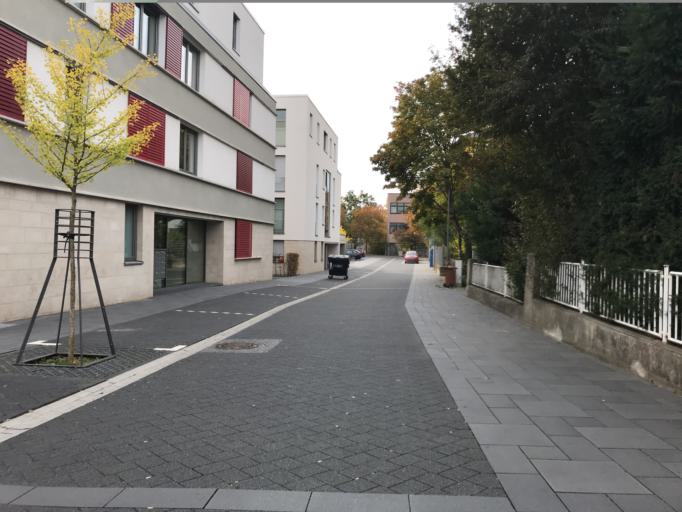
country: DE
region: Rheinland-Pfalz
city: Ingelheim am Rhein
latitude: 49.9731
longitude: 8.0551
